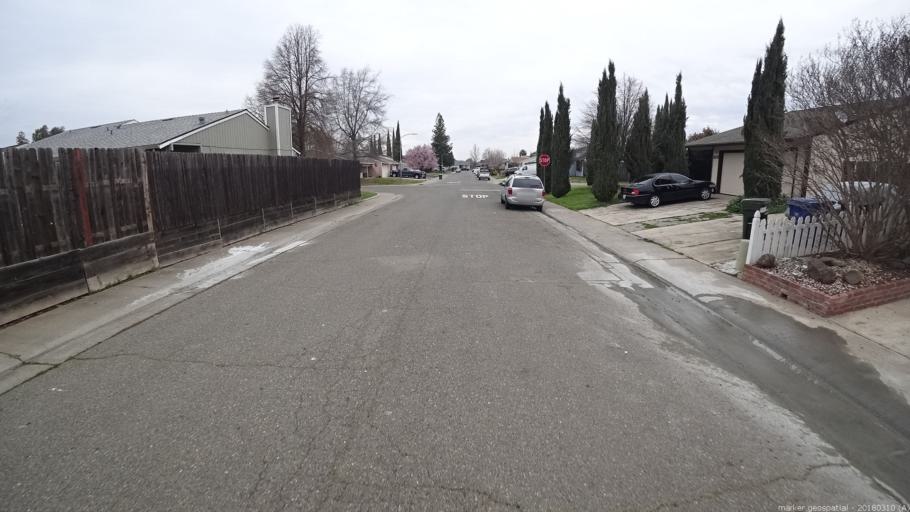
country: US
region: California
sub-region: Sacramento County
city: Vineyard
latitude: 38.4758
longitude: -121.3792
